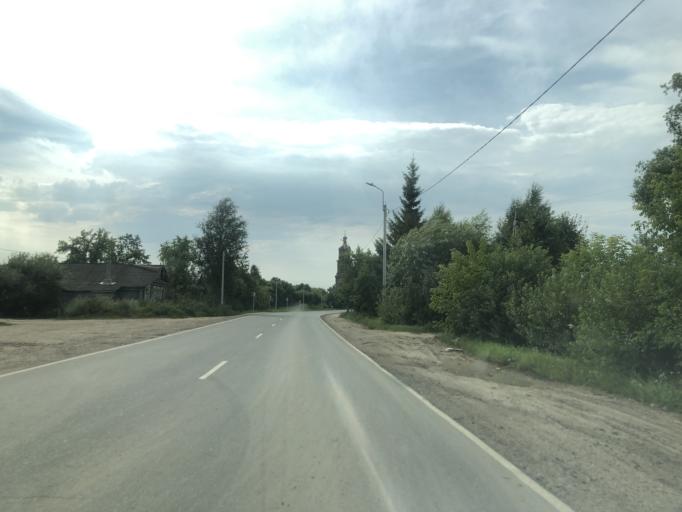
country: RU
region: Ivanovo
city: Shuya
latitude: 56.8536
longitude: 41.5530
